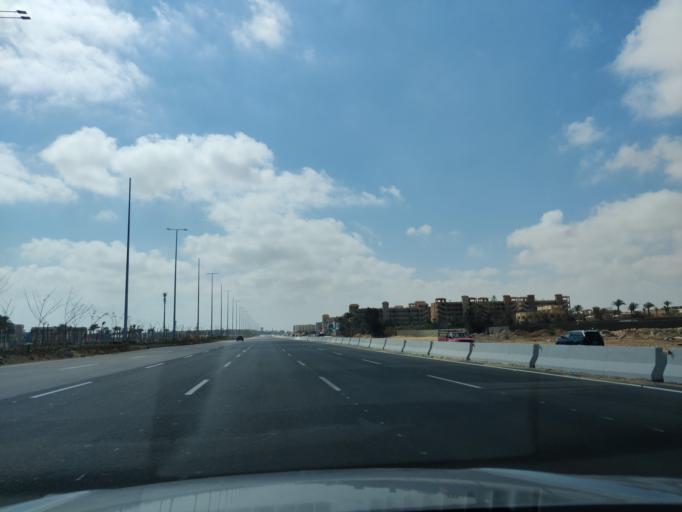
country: EG
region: Muhafazat Matruh
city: Al `Alamayn
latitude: 30.9623
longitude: 28.7547
